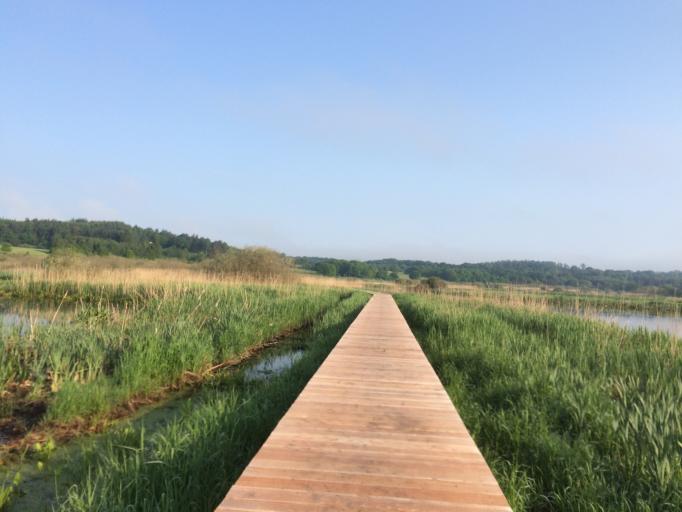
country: DK
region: Central Jutland
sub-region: Silkeborg Kommune
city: Svejbaek
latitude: 56.1955
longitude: 9.6526
